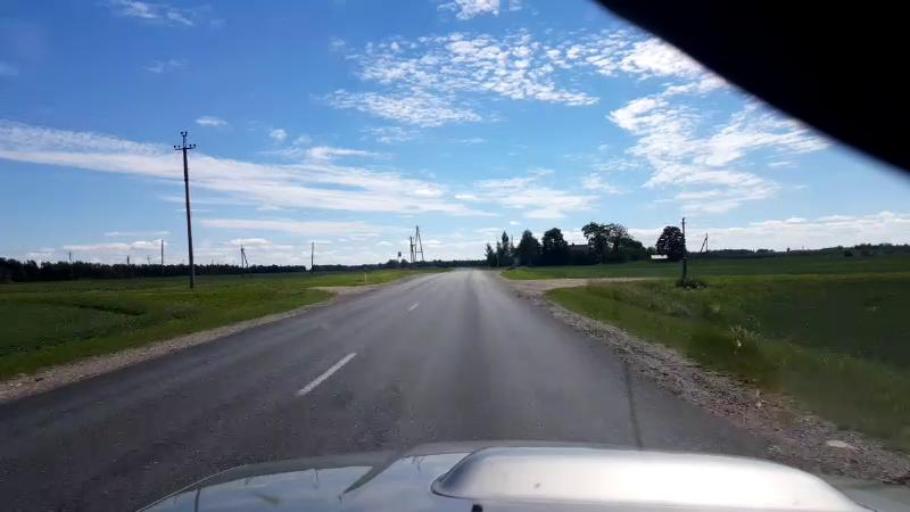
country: EE
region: Laeaene-Virumaa
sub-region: Rakke vald
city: Rakke
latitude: 58.8992
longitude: 26.2827
